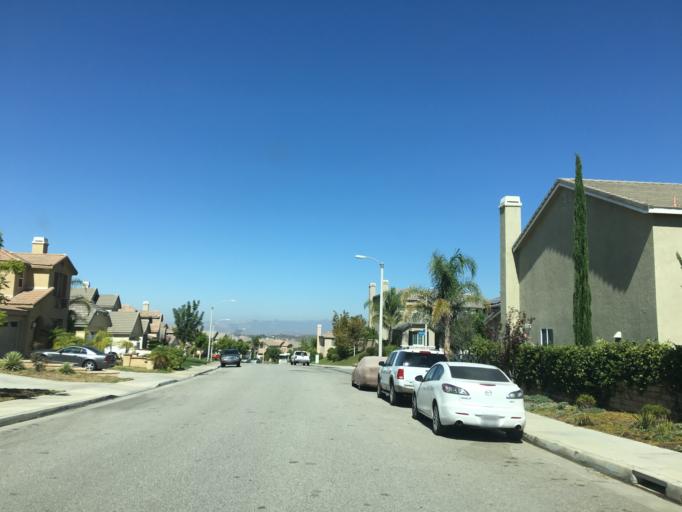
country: US
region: California
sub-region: Los Angeles County
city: Santa Clarita
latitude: 34.4478
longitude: -118.4773
